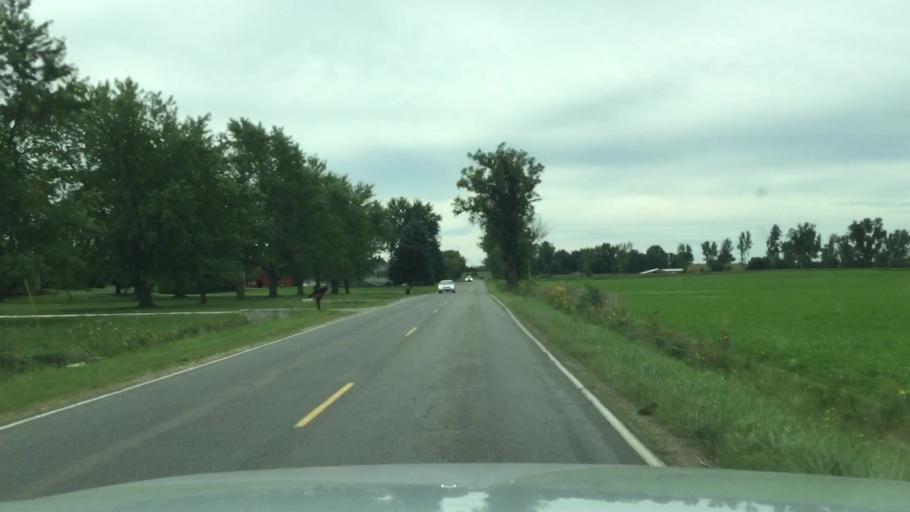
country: US
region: Michigan
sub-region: Shiawassee County
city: Durand
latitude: 42.9629
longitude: -83.9870
